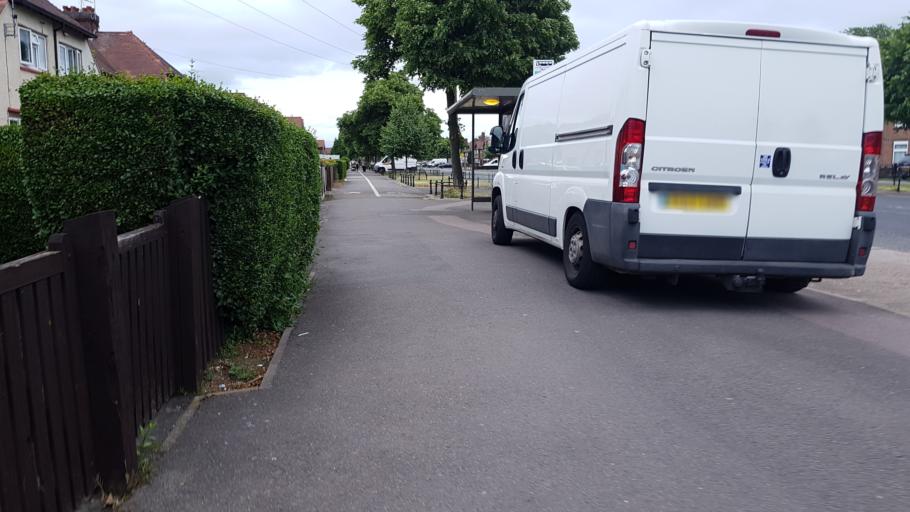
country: GB
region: England
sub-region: Derby
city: Derby
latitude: 52.8931
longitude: -1.4394
